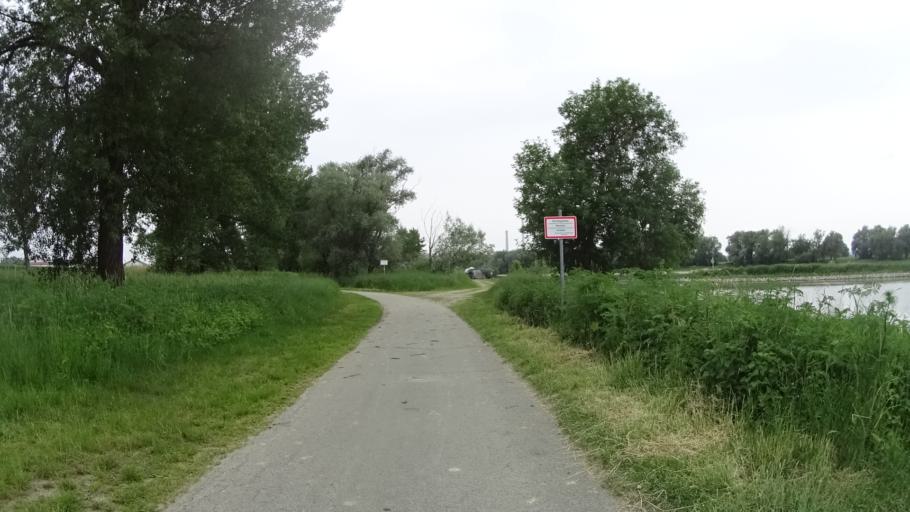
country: DE
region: Bavaria
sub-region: Lower Bavaria
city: Hofkirchen
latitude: 48.6860
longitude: 13.1134
